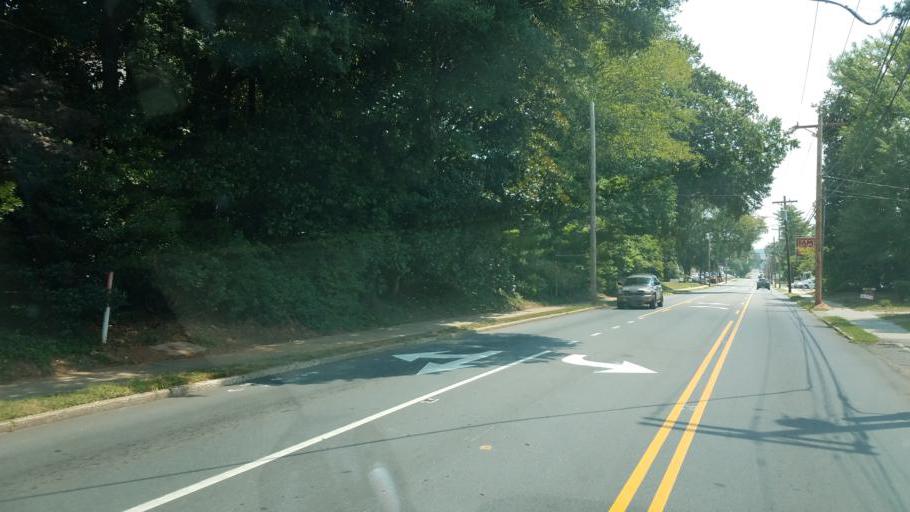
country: US
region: North Carolina
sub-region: Cleveland County
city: Kings Mountain
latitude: 35.2409
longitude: -81.3424
